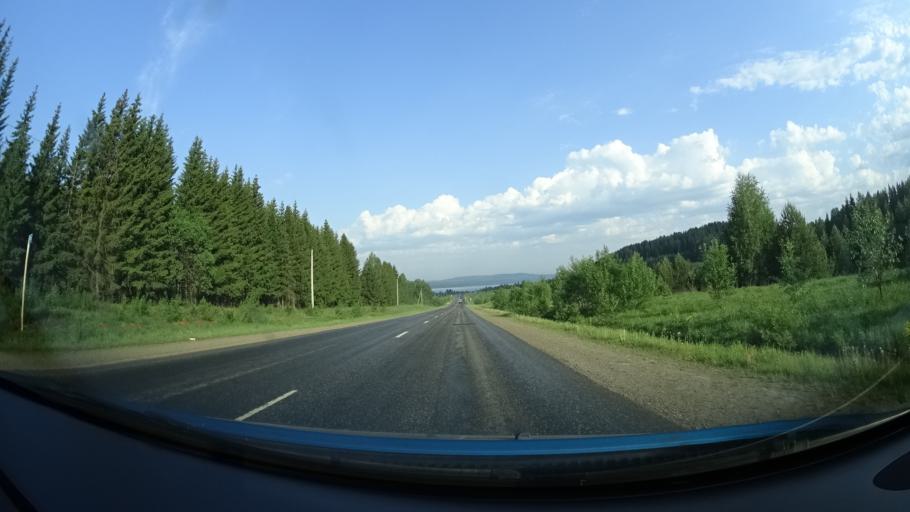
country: RU
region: Perm
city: Osa
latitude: 57.3263
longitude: 55.5996
